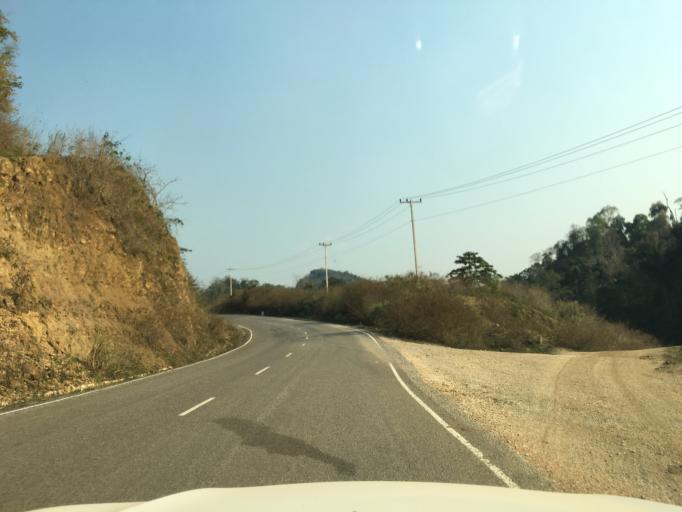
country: LA
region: Houaphan
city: Xam Nua
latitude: 20.5699
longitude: 104.0504
